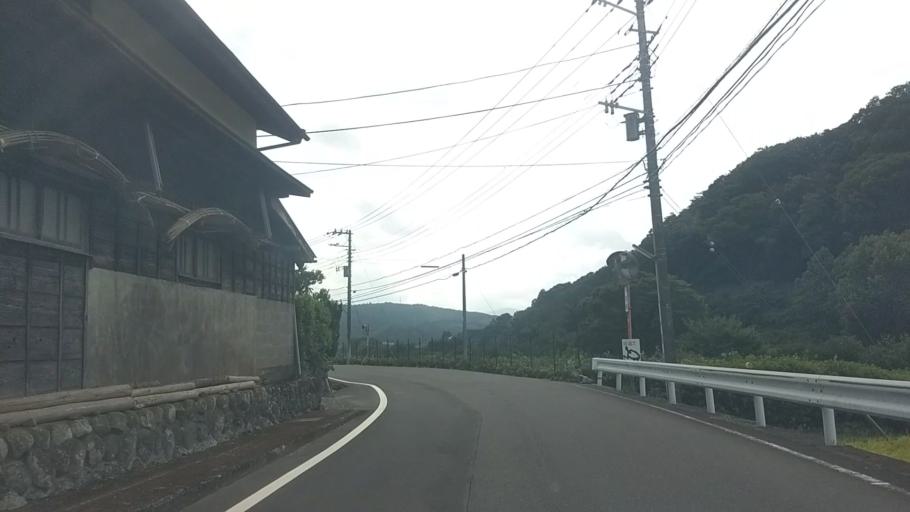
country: JP
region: Shizuoka
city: Ito
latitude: 34.9787
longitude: 138.9786
